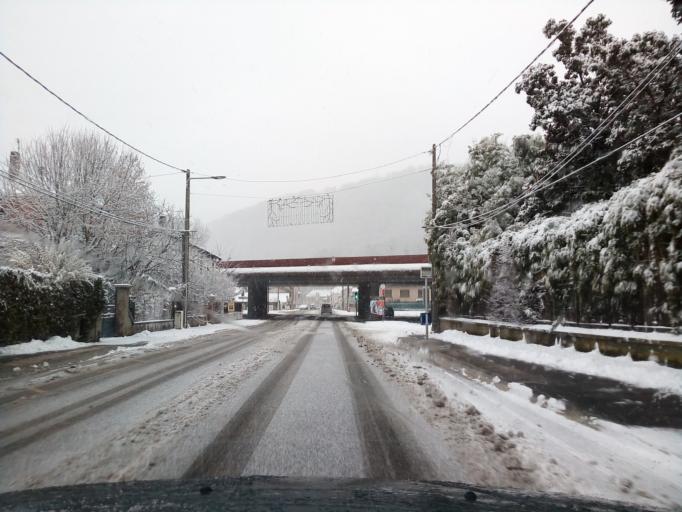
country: FR
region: Rhone-Alpes
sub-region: Departement de l'Isere
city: Saint-Martin-d'Heres
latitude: 45.1788
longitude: 5.7730
